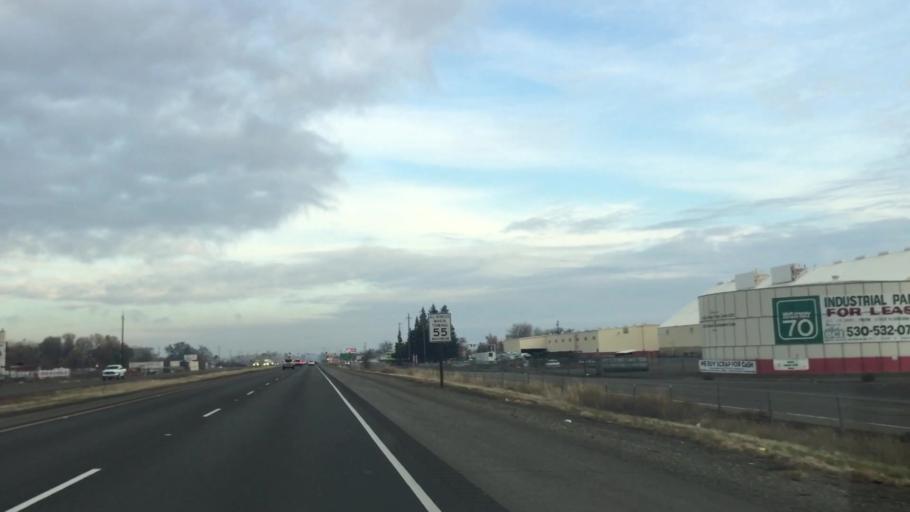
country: US
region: California
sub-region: Butte County
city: South Oroville
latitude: 39.4713
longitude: -121.5756
